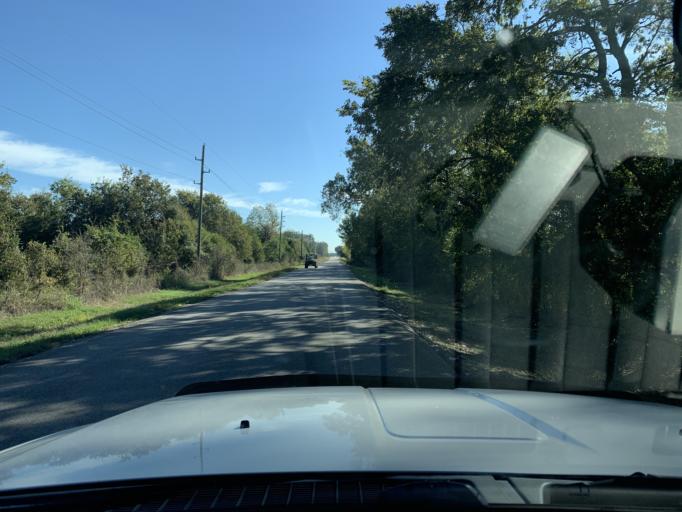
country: US
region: Texas
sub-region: Fort Bend County
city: Rosenberg
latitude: 29.6212
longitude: -95.8291
